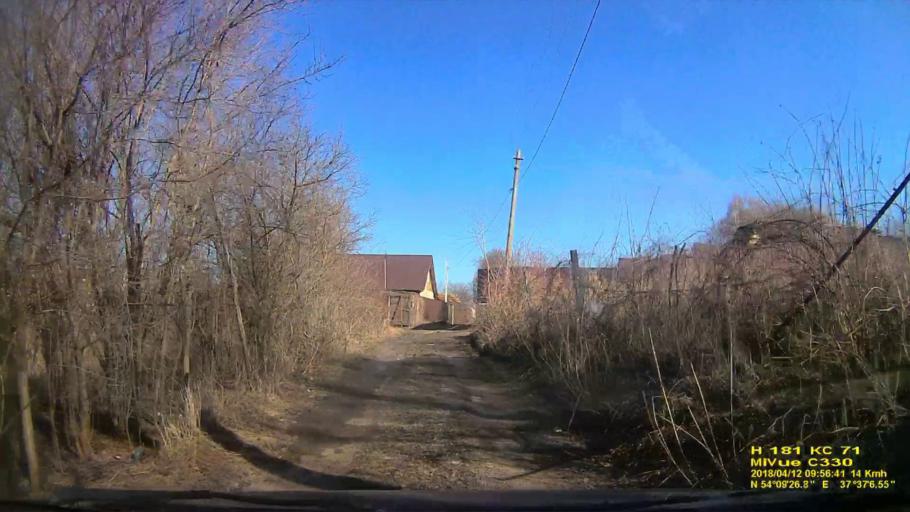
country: RU
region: Tula
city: Mendeleyevskiy
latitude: 54.1575
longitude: 37.6185
